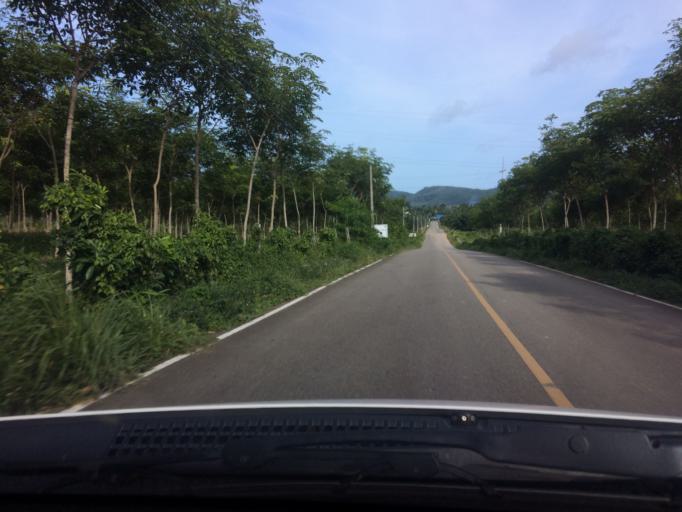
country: TH
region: Phuket
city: Thalang
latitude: 8.0432
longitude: 98.3346
